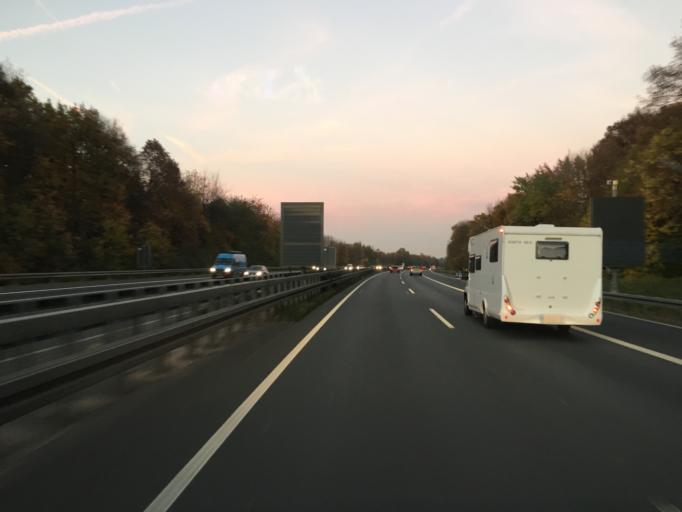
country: DE
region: North Rhine-Westphalia
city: Schwerte
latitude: 51.3979
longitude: 7.5316
